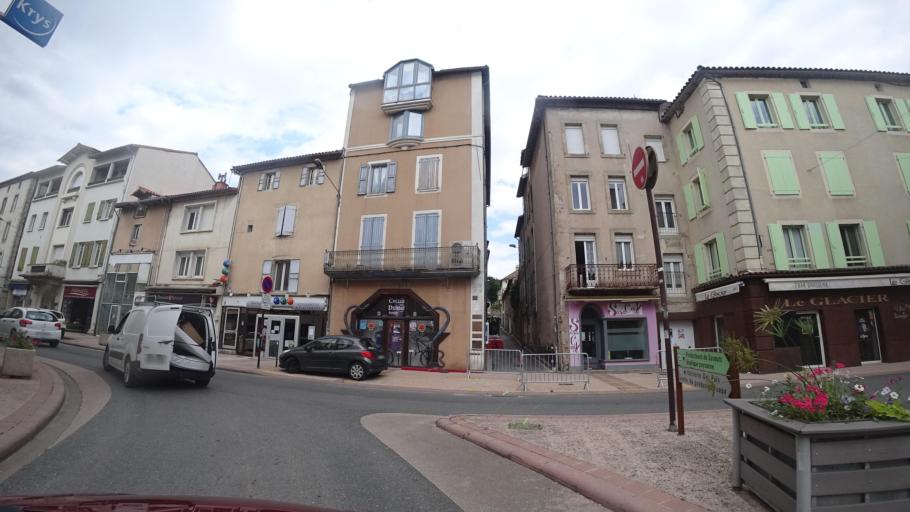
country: FR
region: Midi-Pyrenees
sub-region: Departement de l'Aveyron
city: Saint-Affrique
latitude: 43.9581
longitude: 2.8876
